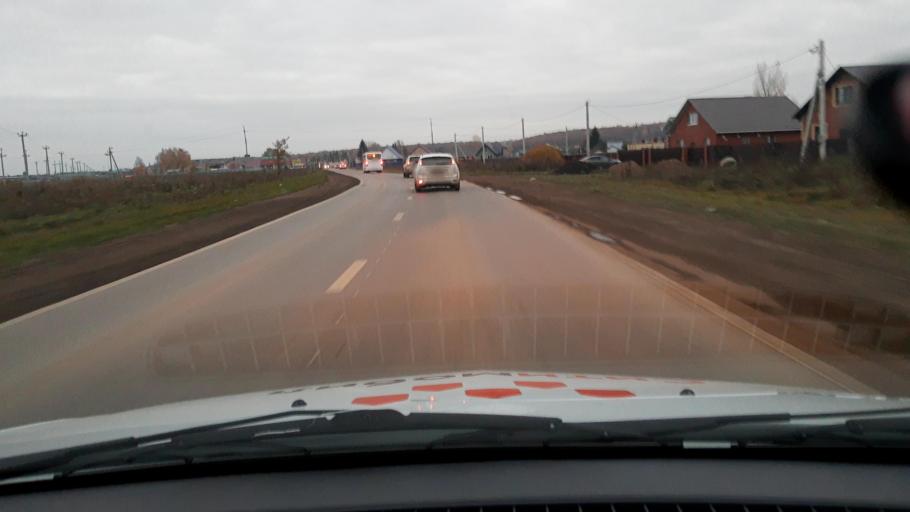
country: RU
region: Bashkortostan
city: Kabakovo
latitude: 54.6841
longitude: 56.1301
